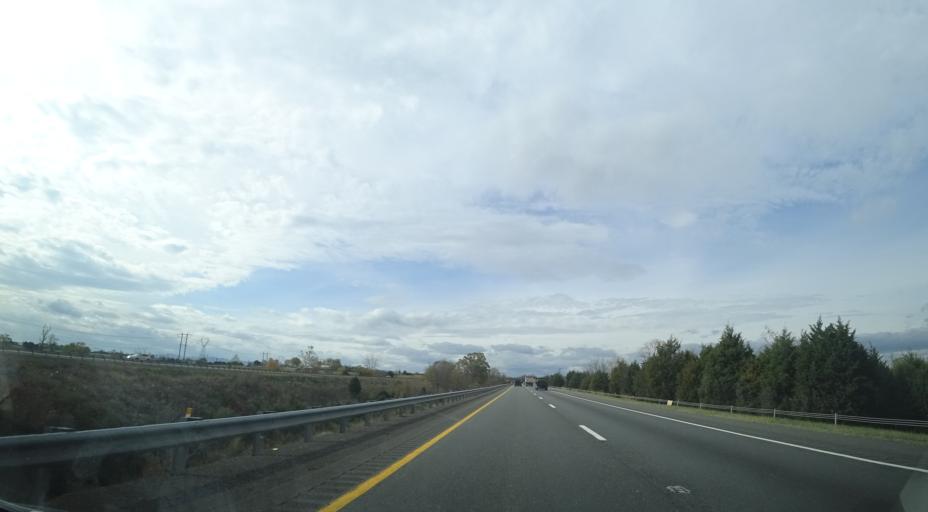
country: US
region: Virginia
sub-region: Warren County
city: Apple Mountain Lake
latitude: 38.9435
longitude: -78.1400
